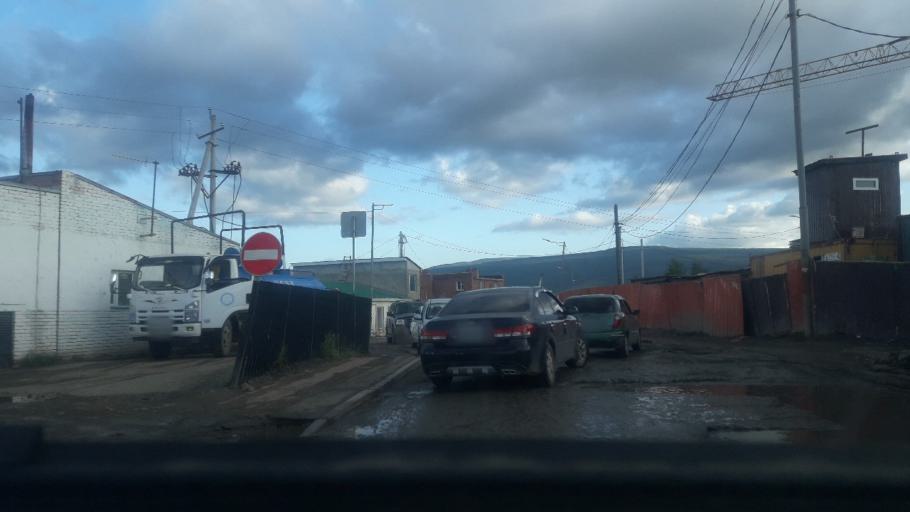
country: MN
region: Ulaanbaatar
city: Ulaanbaatar
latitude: 47.9215
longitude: 106.9953
